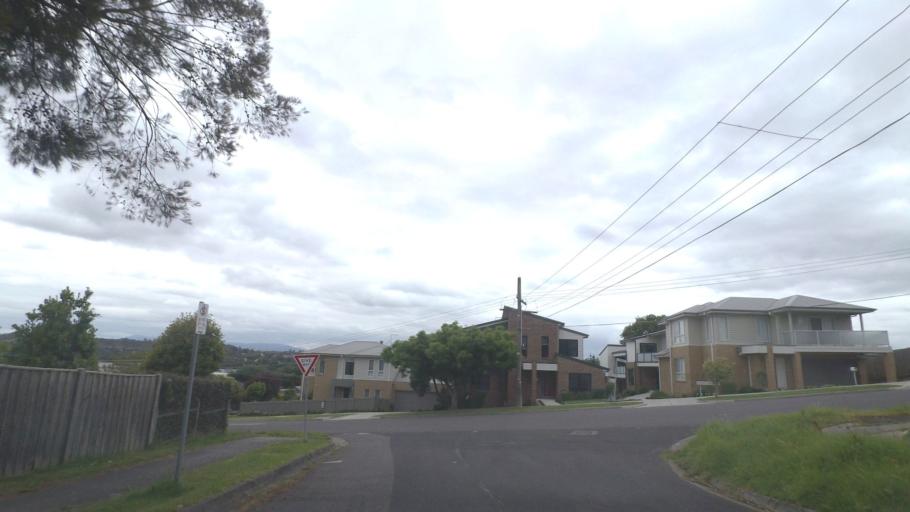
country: AU
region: Victoria
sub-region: Yarra Ranges
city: Lilydale
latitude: -37.7556
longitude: 145.3401
